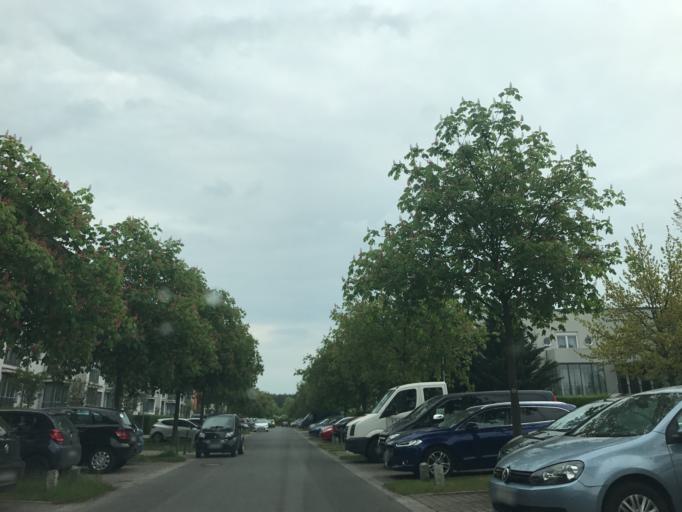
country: DE
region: Berlin
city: Staaken
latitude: 52.5594
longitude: 13.1376
